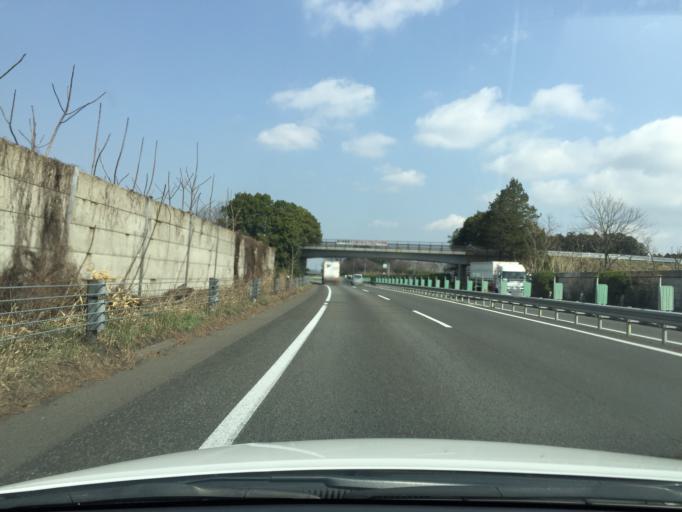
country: JP
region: Miyagi
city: Shiroishi
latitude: 38.0543
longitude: 140.6532
